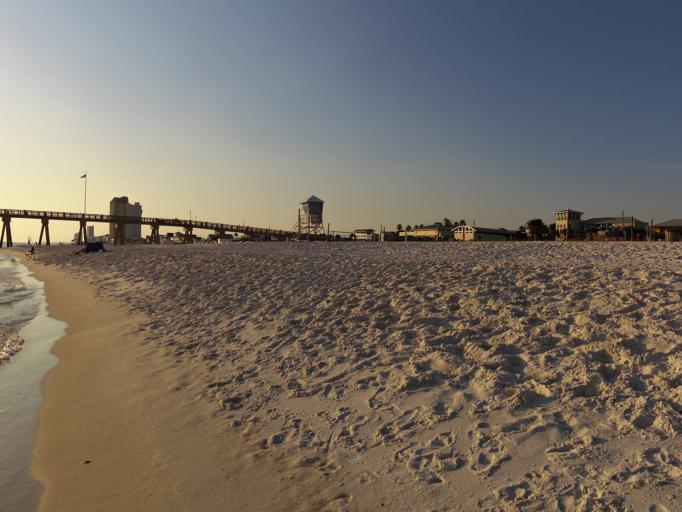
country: US
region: Florida
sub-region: Bay County
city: Laguna Beach
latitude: 30.2142
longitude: -85.8765
